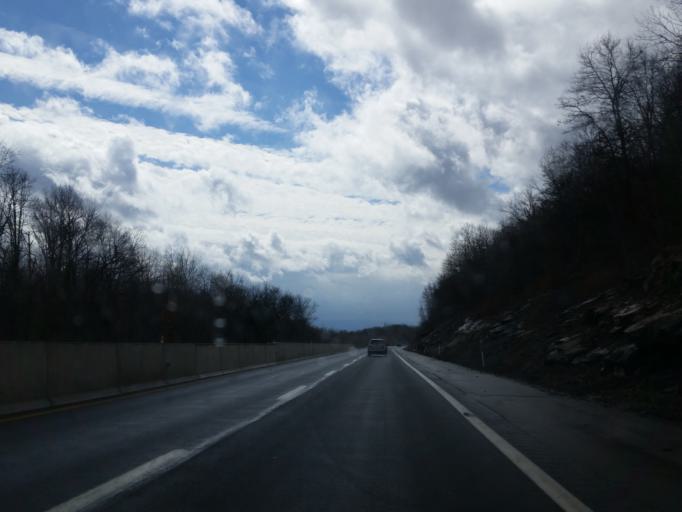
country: US
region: Pennsylvania
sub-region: Lackawanna County
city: Chinchilla
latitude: 41.4491
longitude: -75.6888
